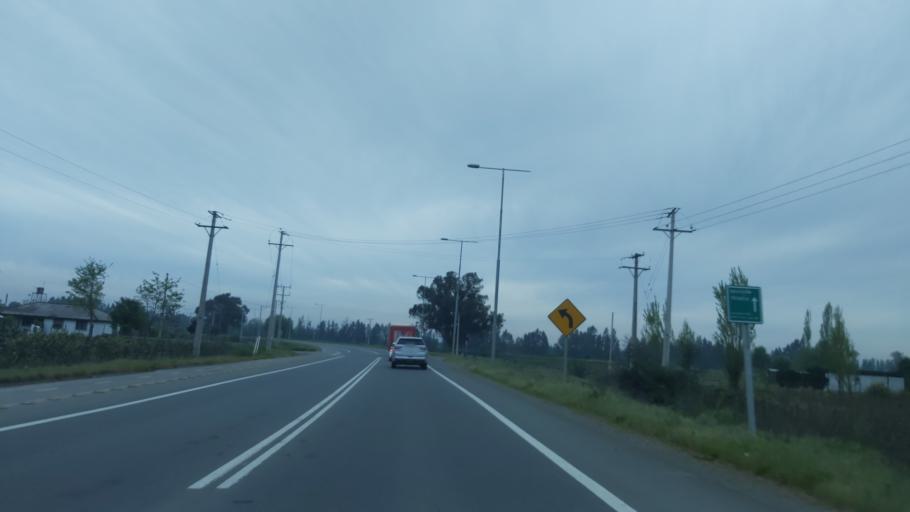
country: CL
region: Maule
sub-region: Provincia de Linares
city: Linares
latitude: -35.8251
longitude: -71.5921
